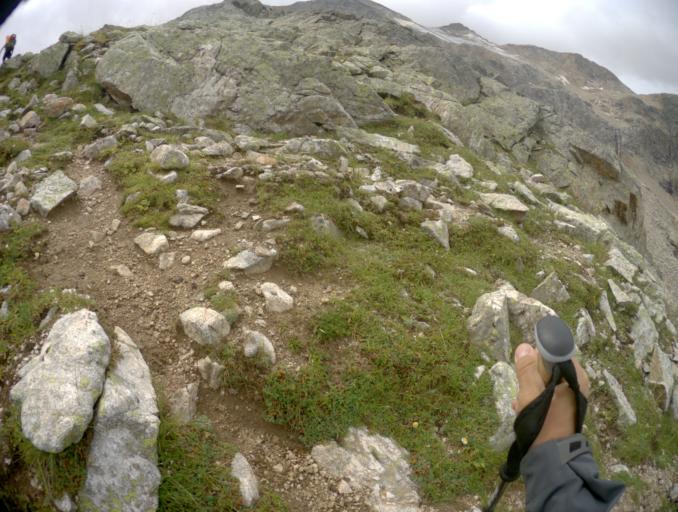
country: RU
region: Karachayevo-Cherkesiya
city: Uchkulan
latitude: 43.2828
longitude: 42.1030
